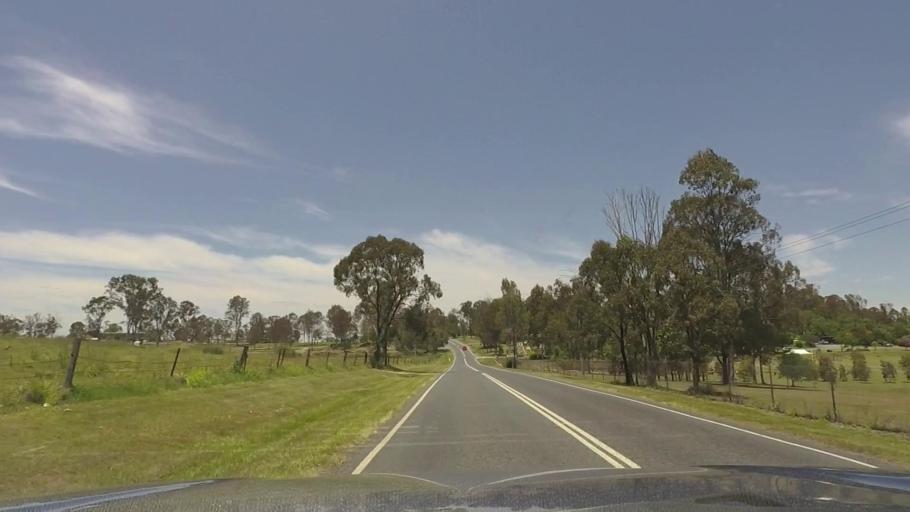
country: AU
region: Queensland
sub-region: Logan
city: North Maclean
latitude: -27.8243
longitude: 153.0264
